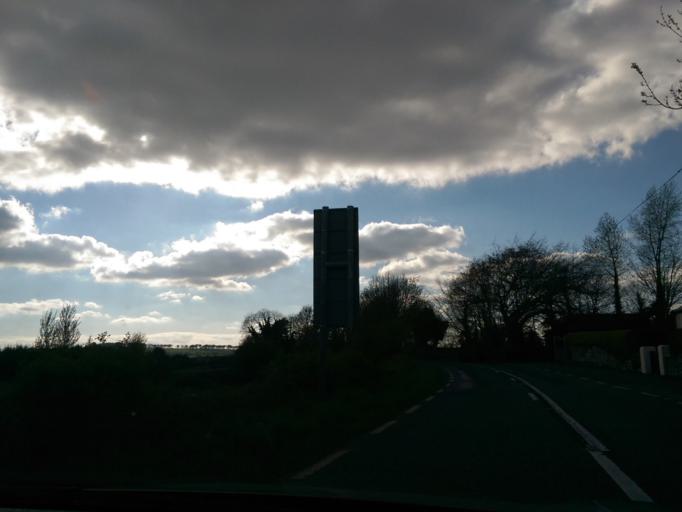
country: IE
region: Connaught
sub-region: County Galway
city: Loughrea
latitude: 53.2008
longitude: -8.4562
